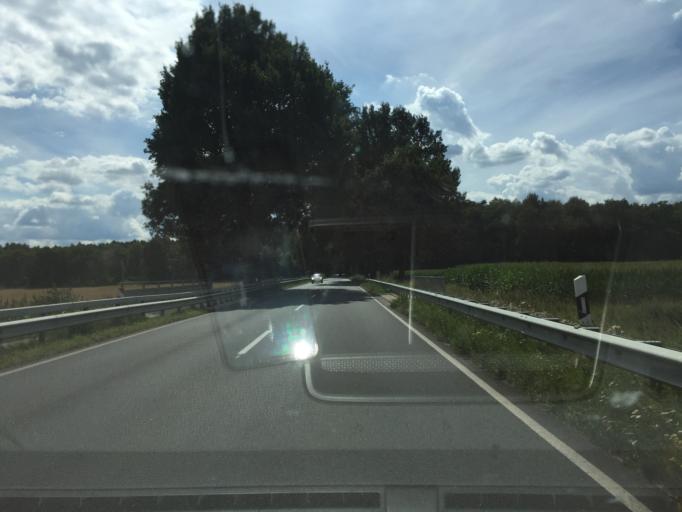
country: DE
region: Lower Saxony
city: Bohme
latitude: 52.8089
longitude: 9.4364
